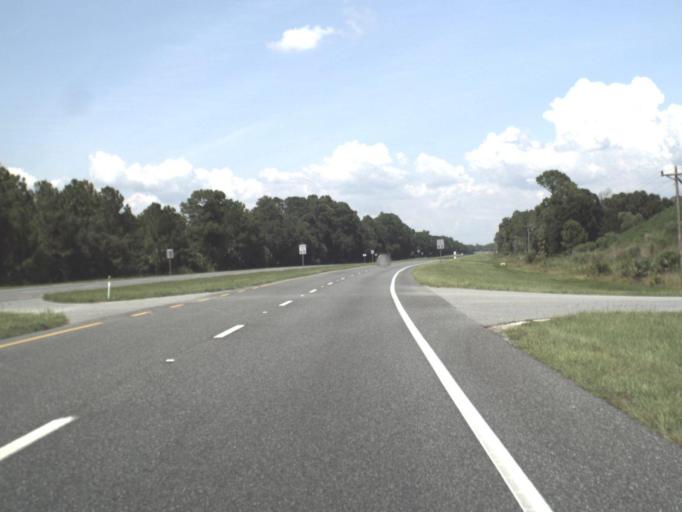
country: US
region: Florida
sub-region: Levy County
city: Inglis
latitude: 29.0425
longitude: -82.6668
